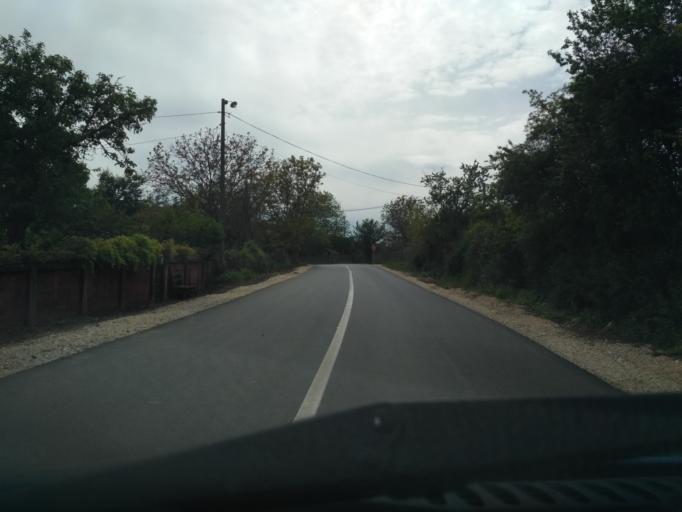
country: RS
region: Central Serbia
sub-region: Podunavski Okrug
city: Velika Plana
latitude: 44.3589
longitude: 21.0305
